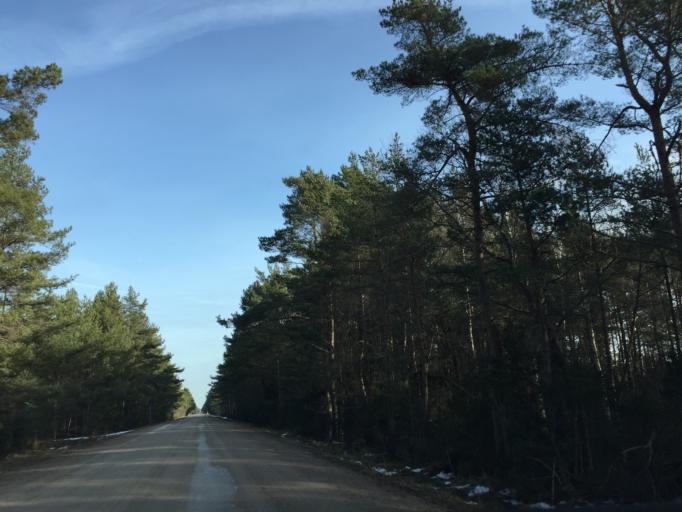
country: EE
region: Saare
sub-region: Kuressaare linn
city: Kuressaare
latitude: 58.2971
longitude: 21.9504
